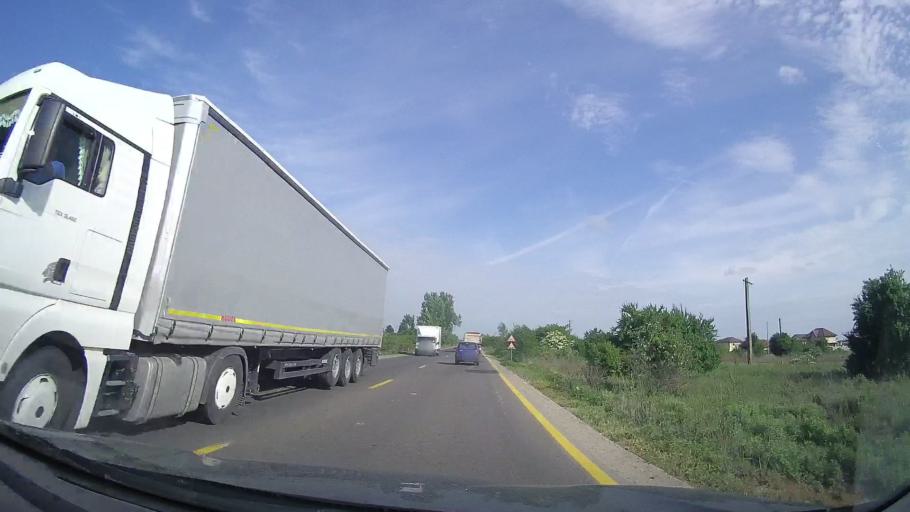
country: RO
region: Ilfov
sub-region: Comuna Magurele
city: Varteju
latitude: 44.3726
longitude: 26.0088
